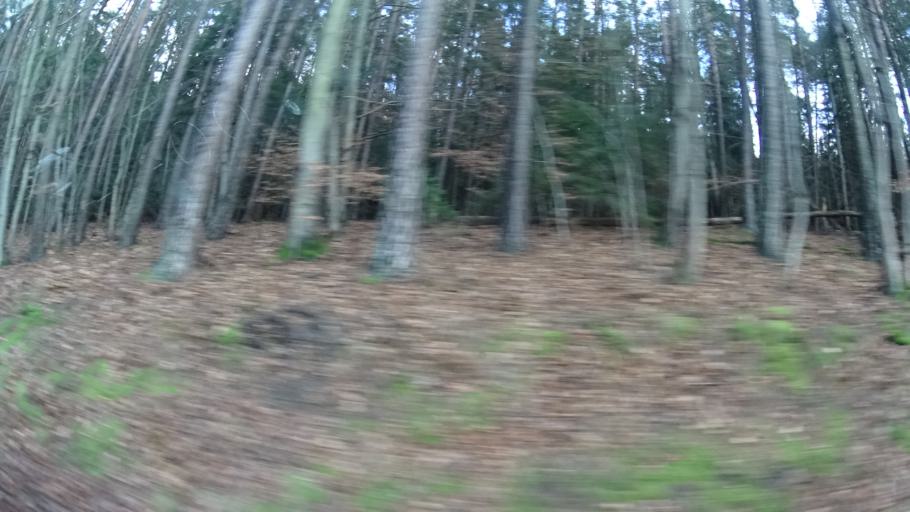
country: DE
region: Thuringia
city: Wernshausen
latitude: 50.7220
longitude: 10.3147
